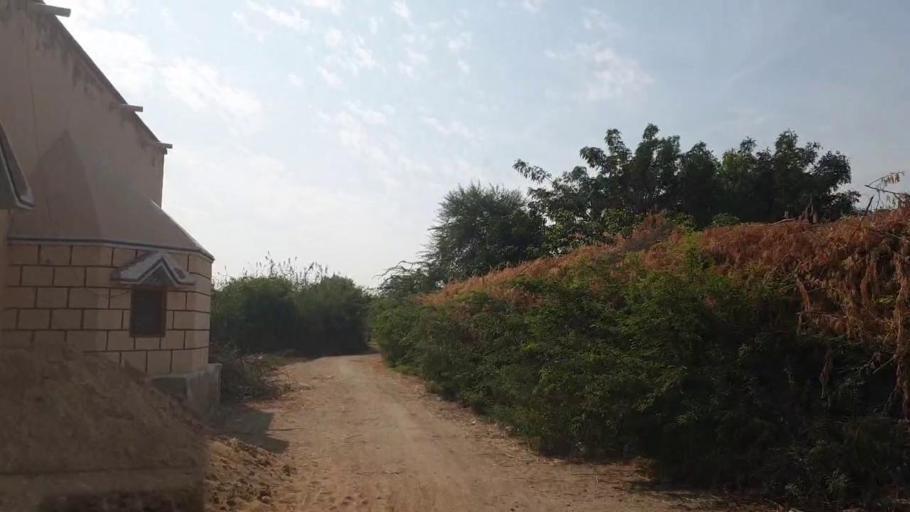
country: PK
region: Sindh
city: Tando Bago
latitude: 24.8837
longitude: 69.0034
